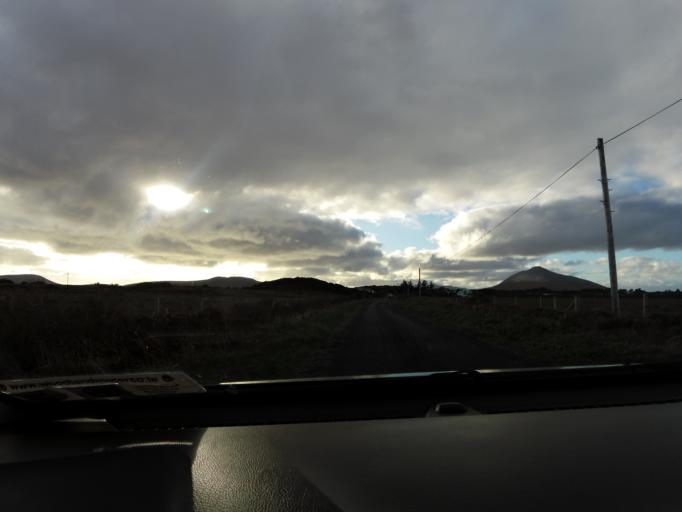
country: IE
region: Connaught
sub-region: Maigh Eo
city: Belmullet
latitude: 53.9958
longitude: -9.9381
